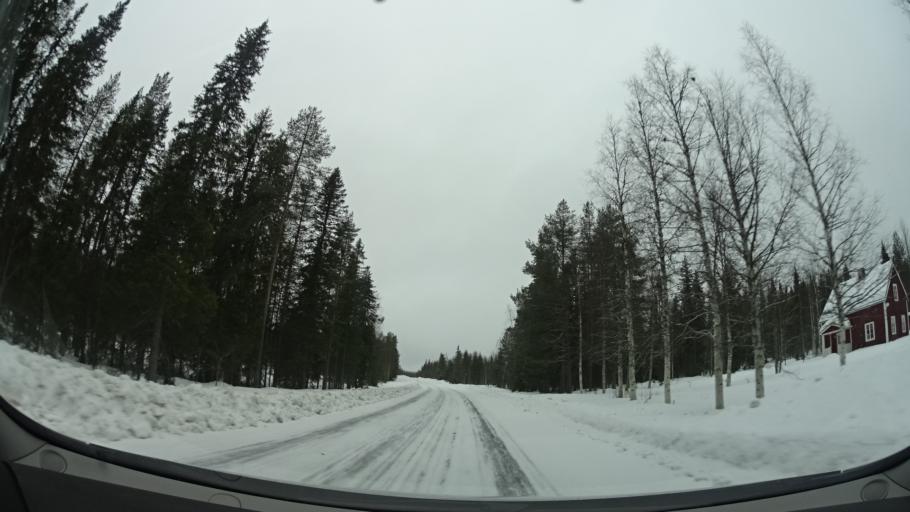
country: SE
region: Vaesterbotten
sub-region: Mala Kommun
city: Mala
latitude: 65.0981
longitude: 18.9166
